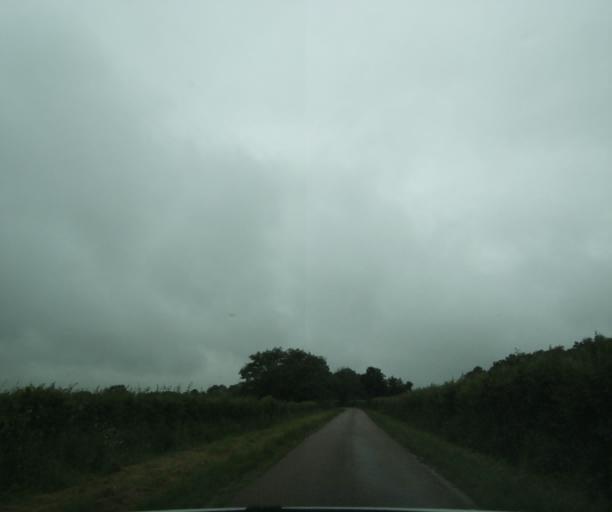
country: FR
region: Bourgogne
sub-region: Departement de Saone-et-Loire
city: Charolles
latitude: 46.4646
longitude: 4.2065
